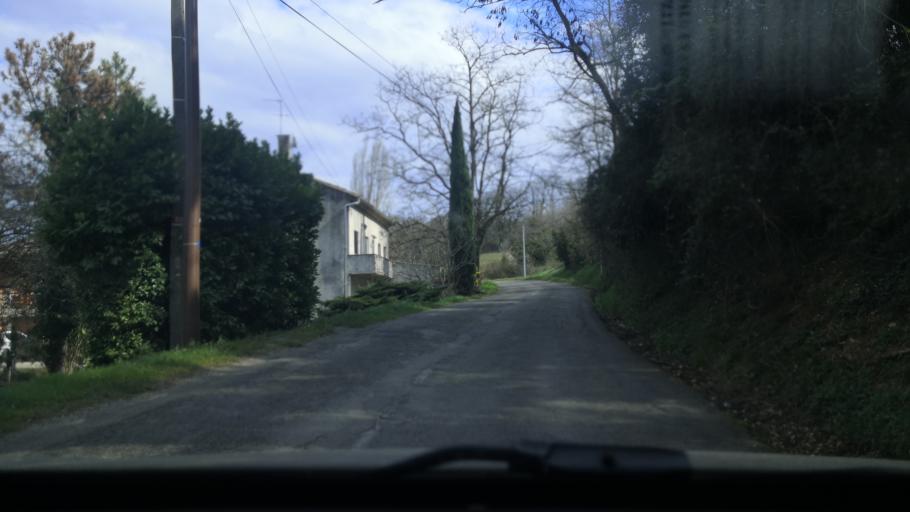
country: FR
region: Rhone-Alpes
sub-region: Departement de la Drome
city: Montelimar
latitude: 44.5737
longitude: 4.7671
